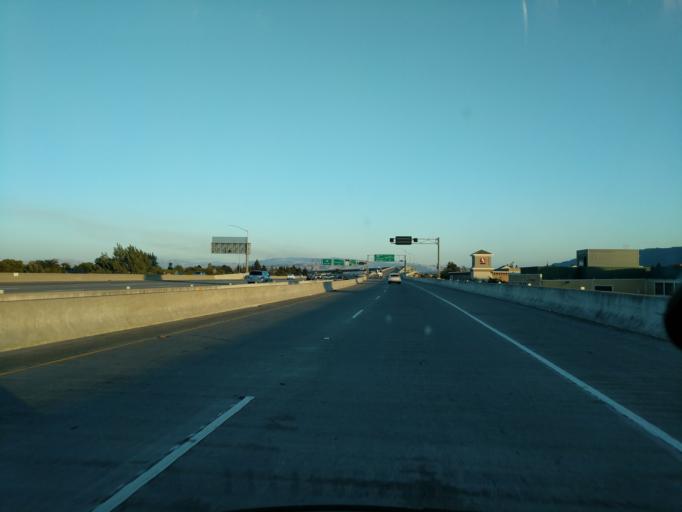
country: US
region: California
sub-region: Alameda County
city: Dublin
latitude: 37.7081
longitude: -121.9279
